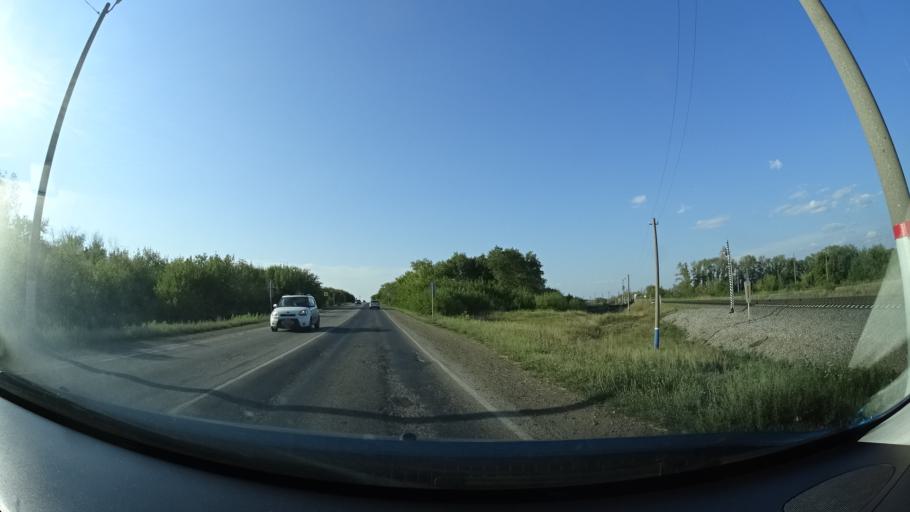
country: RU
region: Bashkortostan
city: Salavat
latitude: 53.4481
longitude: 55.9221
